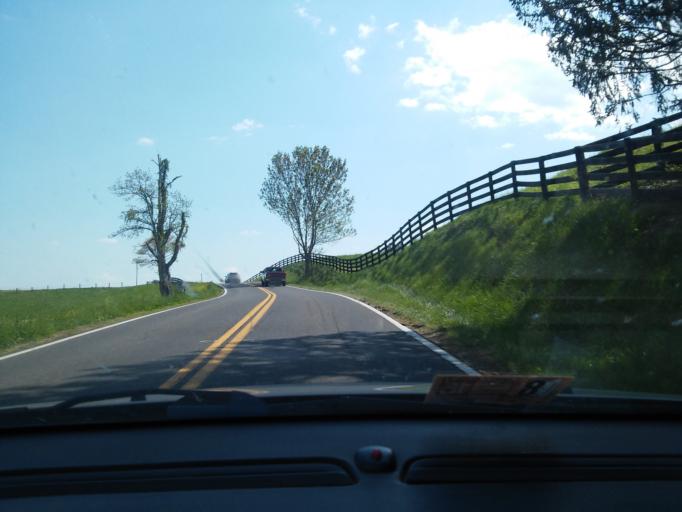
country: US
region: Virginia
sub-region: Rappahannock County
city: Washington
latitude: 38.6063
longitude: -78.2379
